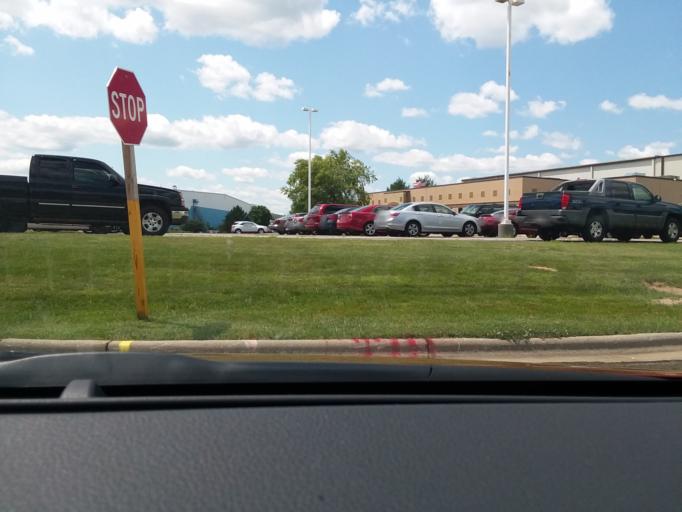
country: US
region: Wisconsin
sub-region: Dane County
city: Windsor
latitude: 43.2002
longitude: -89.3342
